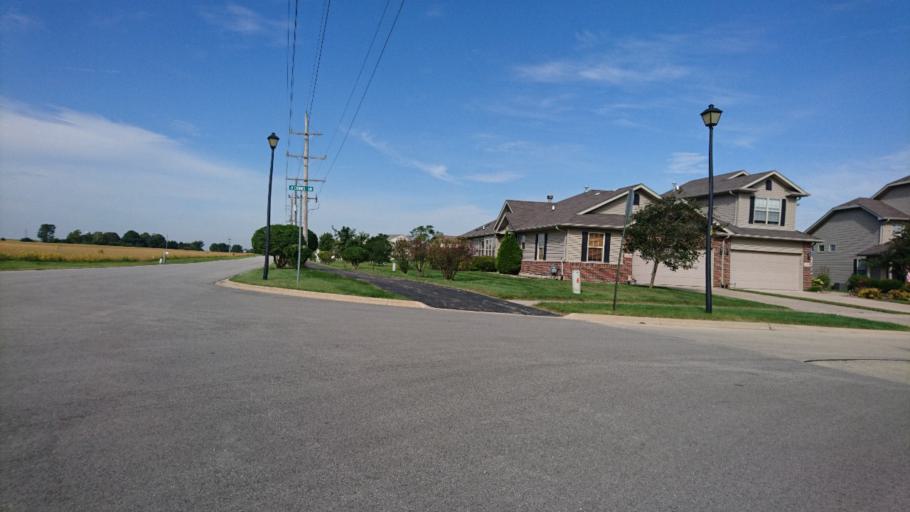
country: US
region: Illinois
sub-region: Will County
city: Manhattan
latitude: 41.4209
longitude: -87.9942
